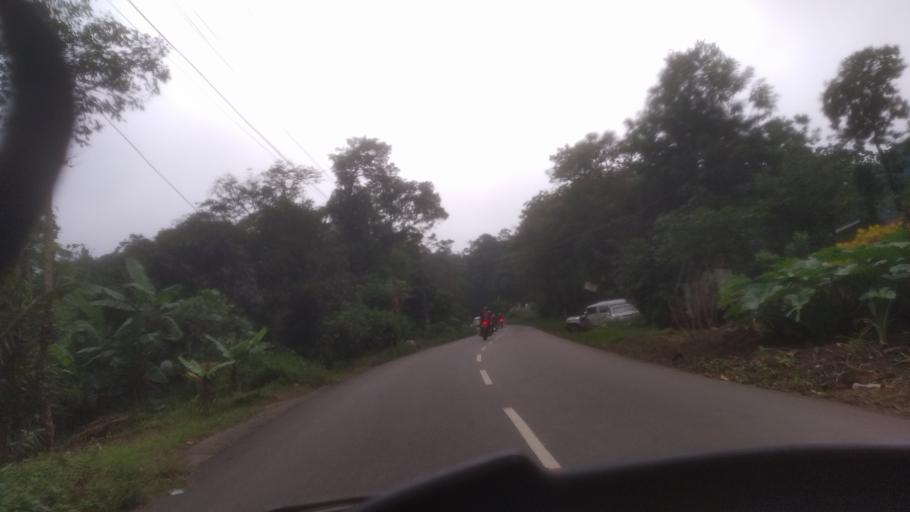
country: IN
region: Tamil Nadu
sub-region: Theni
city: Kombai
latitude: 9.8942
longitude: 77.1978
